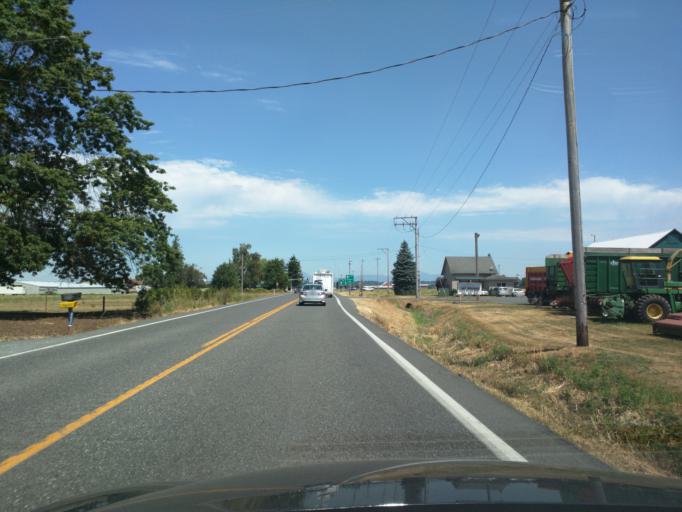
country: US
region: Washington
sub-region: Whatcom County
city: Lynden
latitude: 48.9616
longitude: -122.4852
